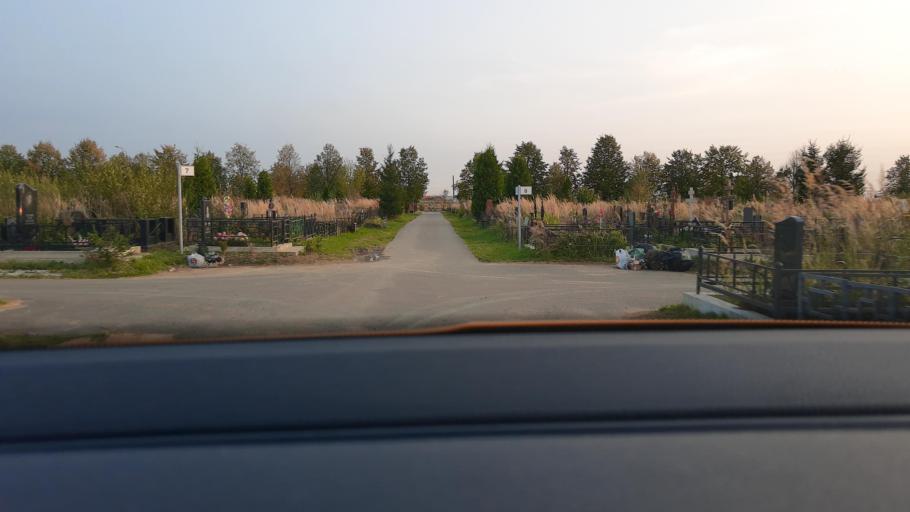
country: RU
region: Moskovskaya
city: Novopodrezkovo
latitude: 56.0076
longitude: 37.3822
